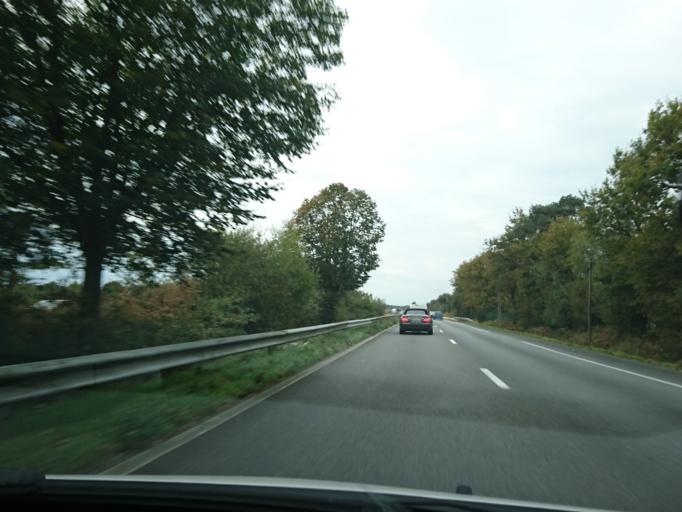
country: FR
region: Pays de la Loire
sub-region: Departement de la Loire-Atlantique
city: Malville
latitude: 47.3490
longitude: -1.8717
